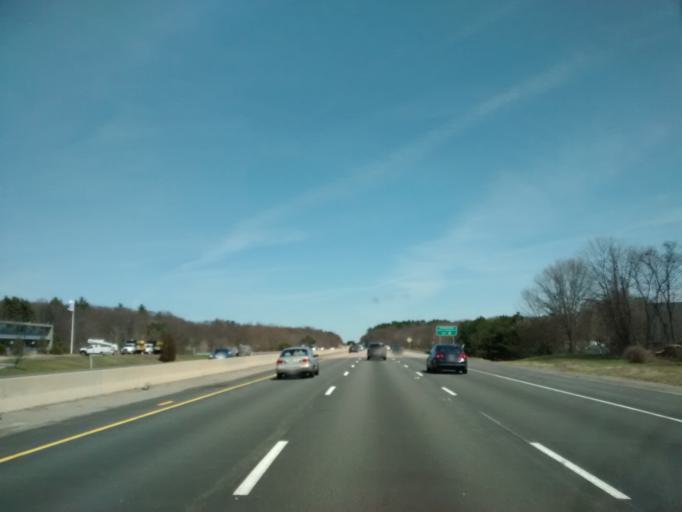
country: US
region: Massachusetts
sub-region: Worcester County
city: Cordaville
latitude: 42.2797
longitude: -71.5181
